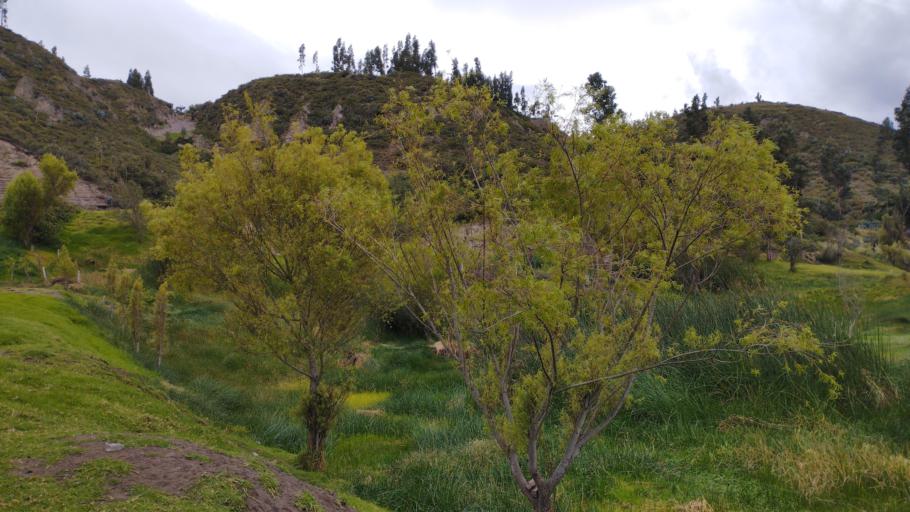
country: EC
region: Chimborazo
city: Guano
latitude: -1.6173
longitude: -78.6093
